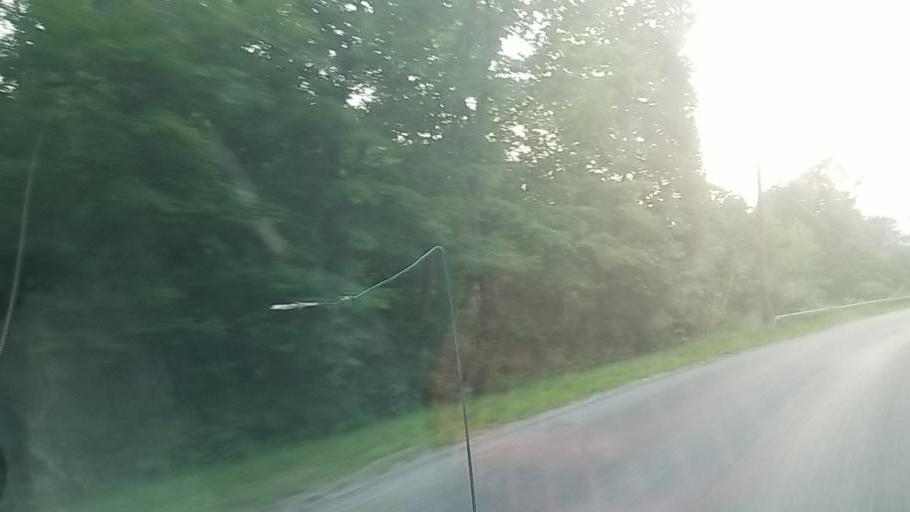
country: US
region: New York
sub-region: Montgomery County
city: Fonda
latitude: 42.9234
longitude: -74.4179
